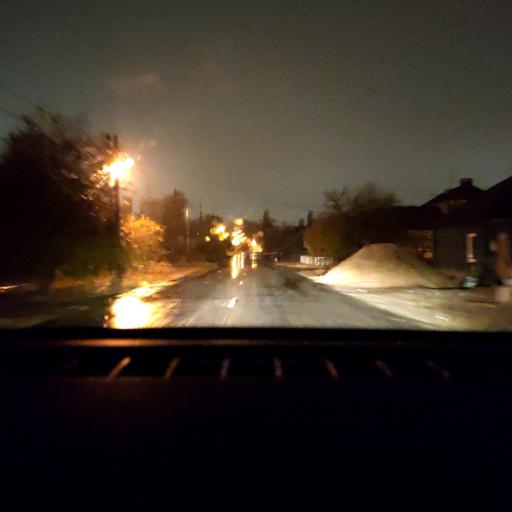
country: RU
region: Voronezj
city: Voronezh
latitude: 51.6661
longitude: 39.2595
